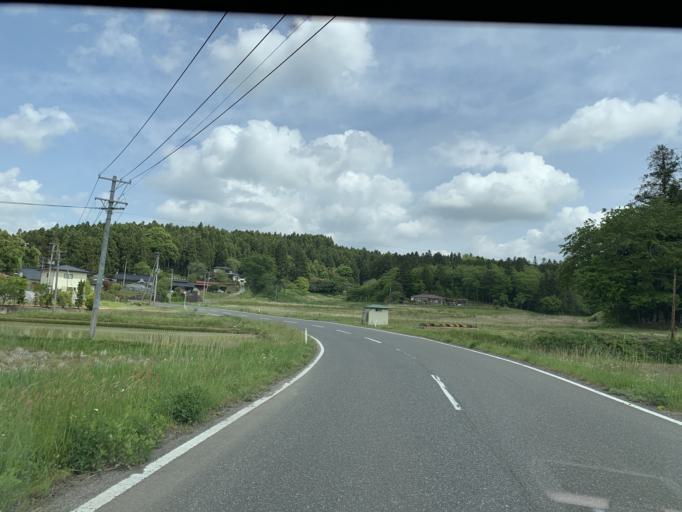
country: JP
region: Iwate
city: Ichinoseki
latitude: 38.8315
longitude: 141.0210
